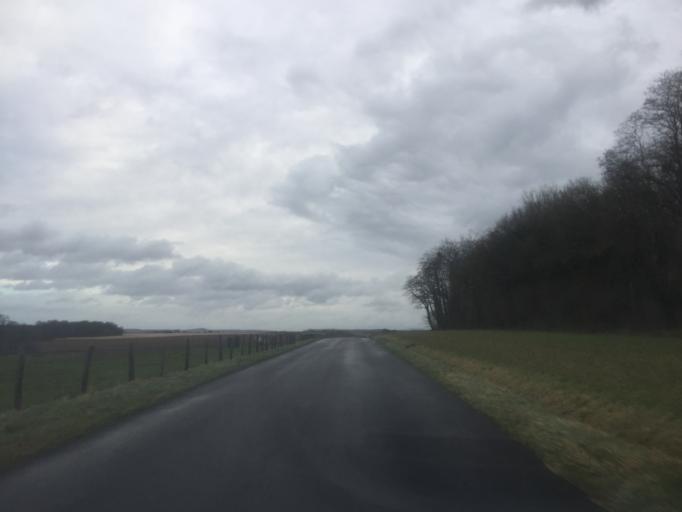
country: FR
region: Franche-Comte
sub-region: Departement de la Haute-Saone
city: Pesmes
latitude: 47.2346
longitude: 5.5854
